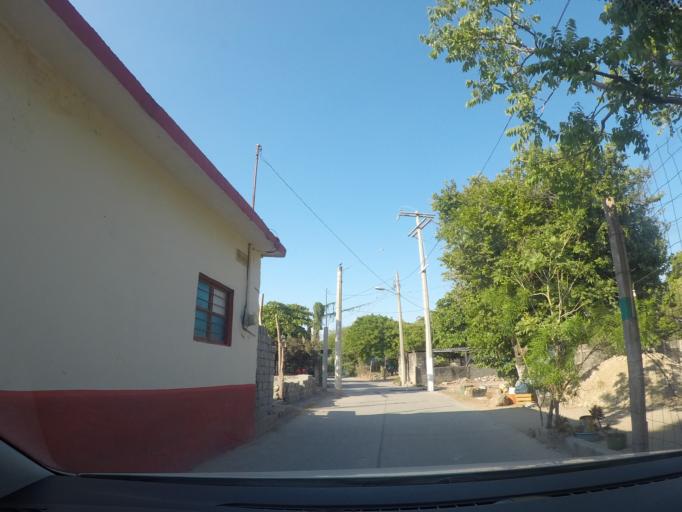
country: MX
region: Oaxaca
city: Juchitan de Zaragoza
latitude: 16.4179
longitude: -95.0254
